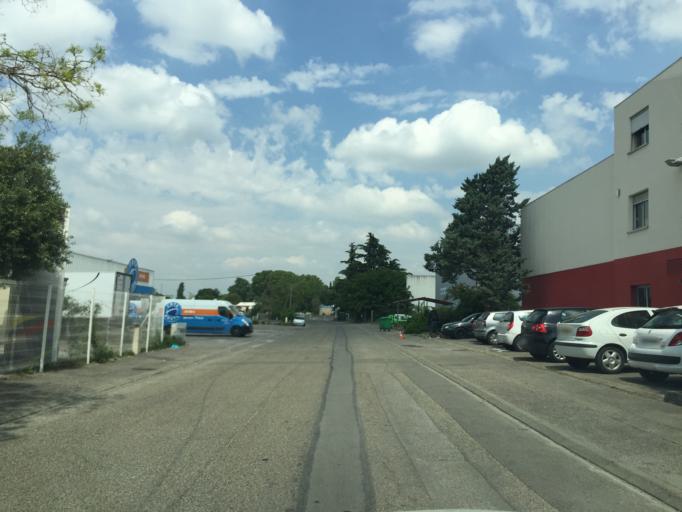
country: FR
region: Provence-Alpes-Cote d'Azur
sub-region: Departement du Vaucluse
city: Montfavet
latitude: 43.9333
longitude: 4.8521
